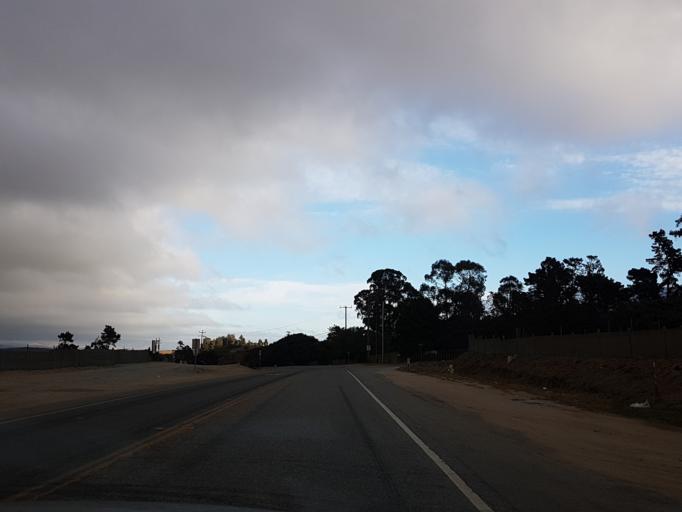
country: US
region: California
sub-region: Monterey County
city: Salinas
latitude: 36.5978
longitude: -121.6261
